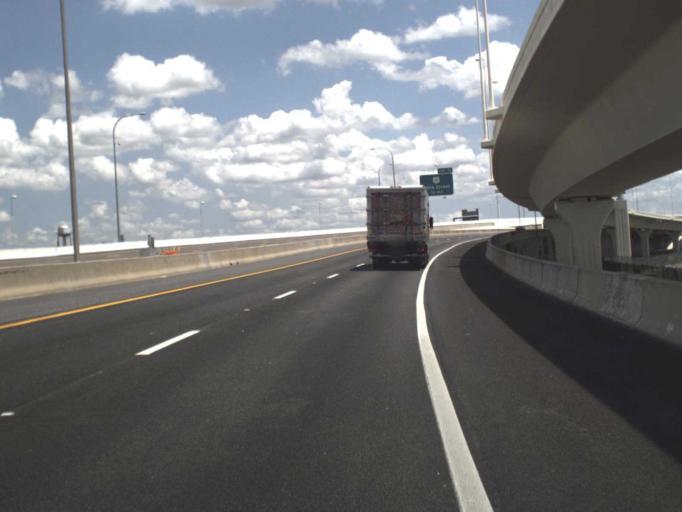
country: US
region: Florida
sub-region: Hillsborough County
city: Tampa
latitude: 27.9542
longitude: -82.4193
